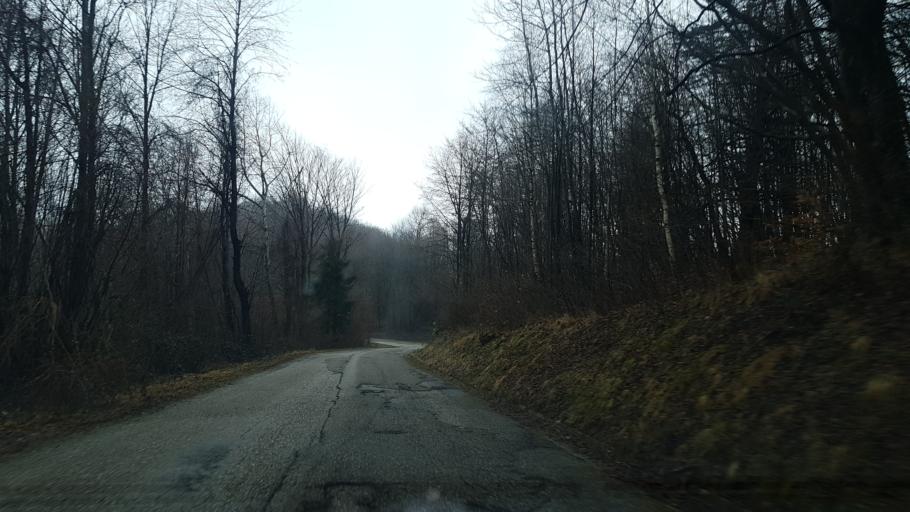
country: IT
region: Friuli Venezia Giulia
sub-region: Provincia di Udine
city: San Leonardo
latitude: 46.1013
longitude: 13.5549
